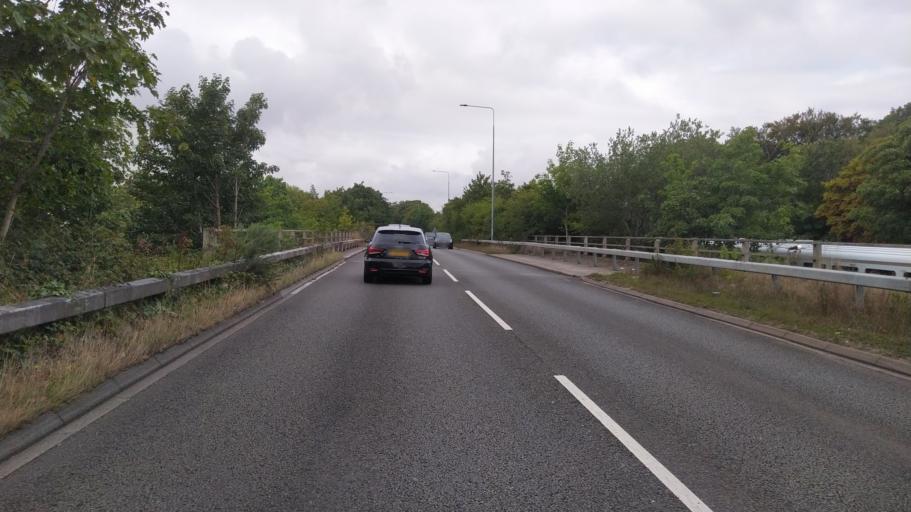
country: GB
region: England
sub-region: Bournemouth
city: Bournemouth
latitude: 50.7241
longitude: -1.9022
